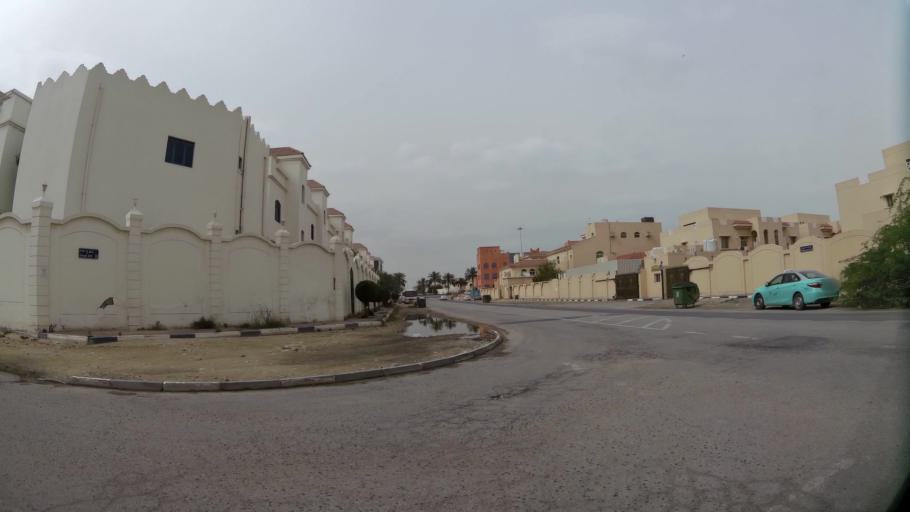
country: QA
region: Baladiyat ad Dawhah
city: Doha
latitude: 25.2523
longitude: 51.5308
